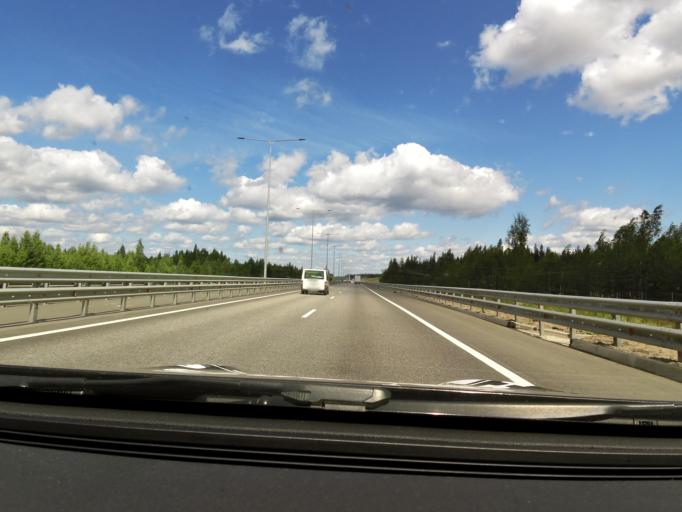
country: RU
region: Tverskaya
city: Krasnomayskiy
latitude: 57.5412
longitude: 34.2721
